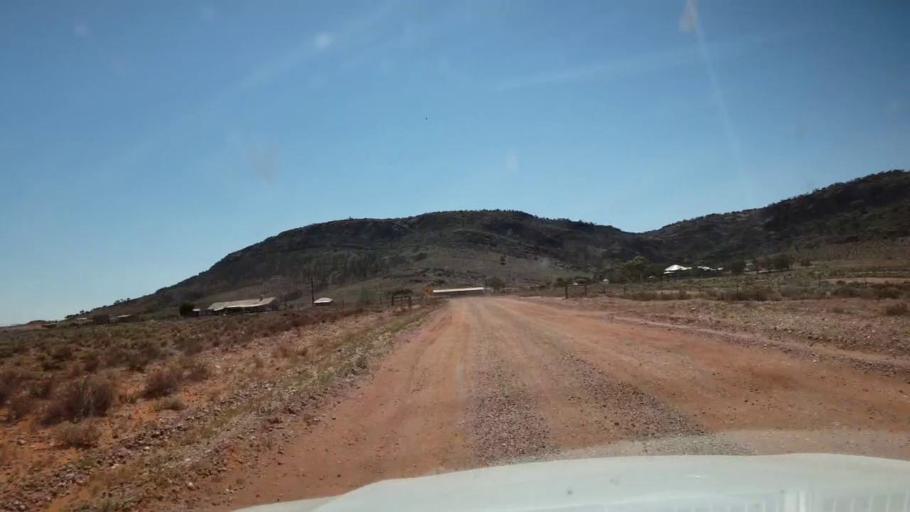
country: AU
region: South Australia
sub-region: Whyalla
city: Whyalla
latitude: -32.6875
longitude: 137.1266
